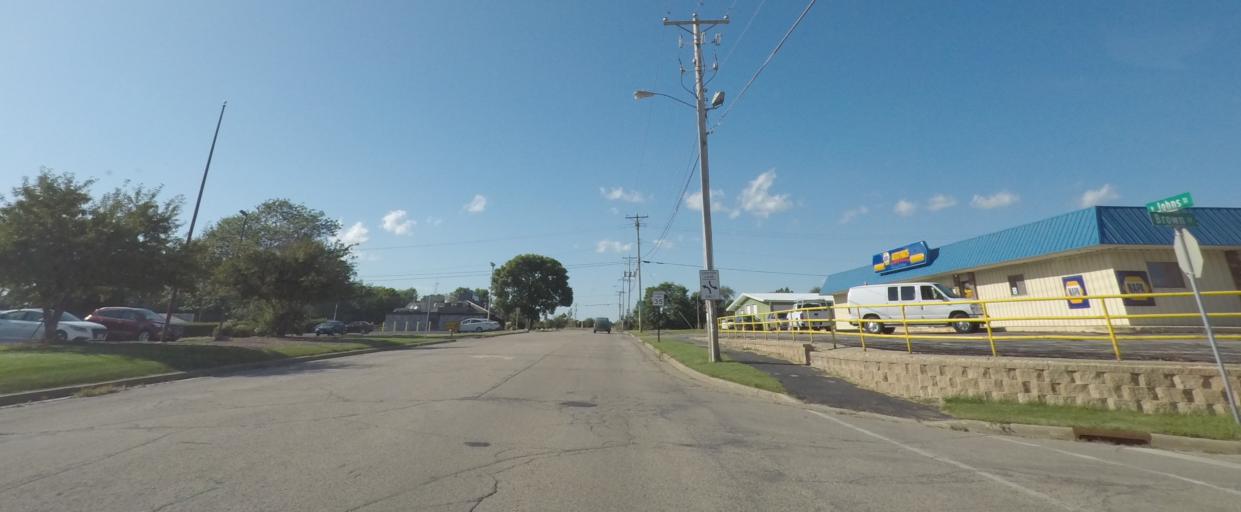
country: US
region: Wisconsin
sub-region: Iowa County
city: Dodgeville
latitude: 42.9763
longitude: -90.1266
